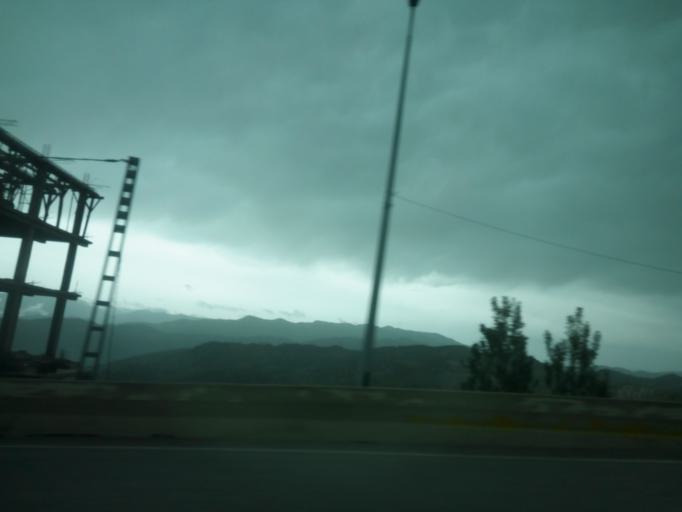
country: DZ
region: Medea
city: Medea
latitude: 36.2695
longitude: 2.7877
